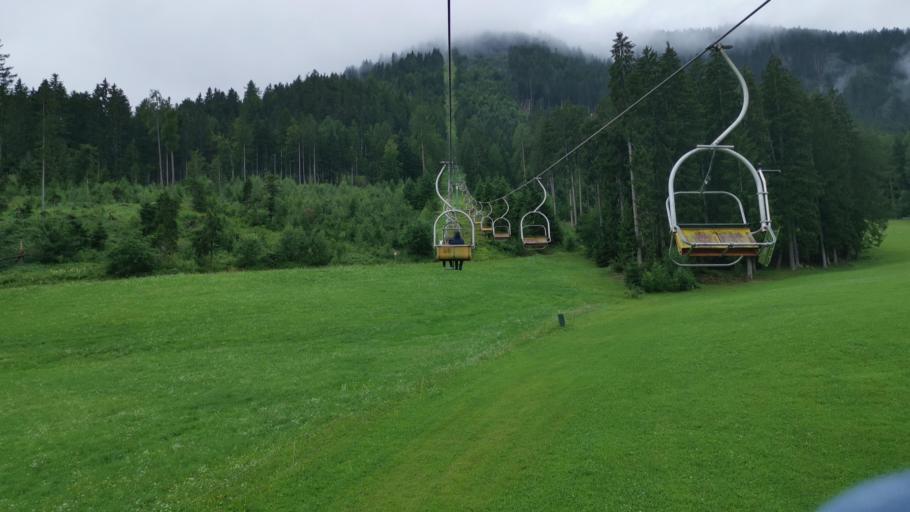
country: AT
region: Tyrol
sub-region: Politischer Bezirk Lienz
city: Leisach
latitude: 46.8257
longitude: 12.7395
